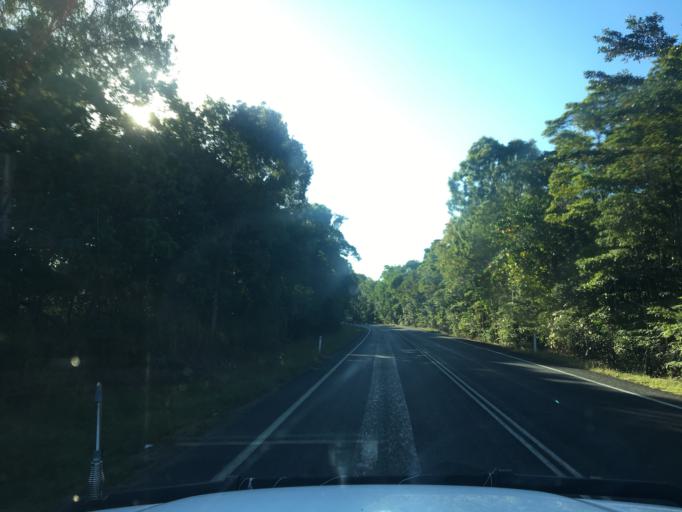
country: AU
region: Queensland
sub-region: Cairns
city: Port Douglas
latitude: -16.5255
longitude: 145.4592
